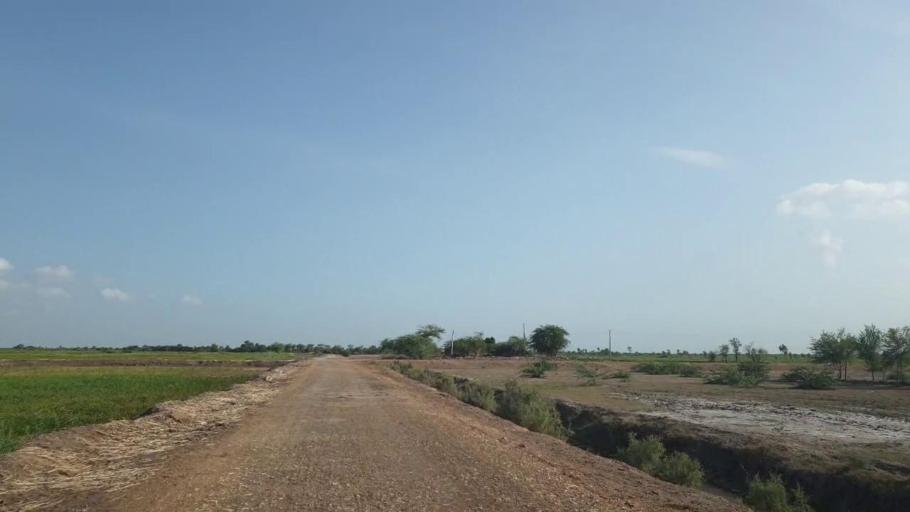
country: PK
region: Sindh
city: Kadhan
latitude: 24.6057
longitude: 69.0879
